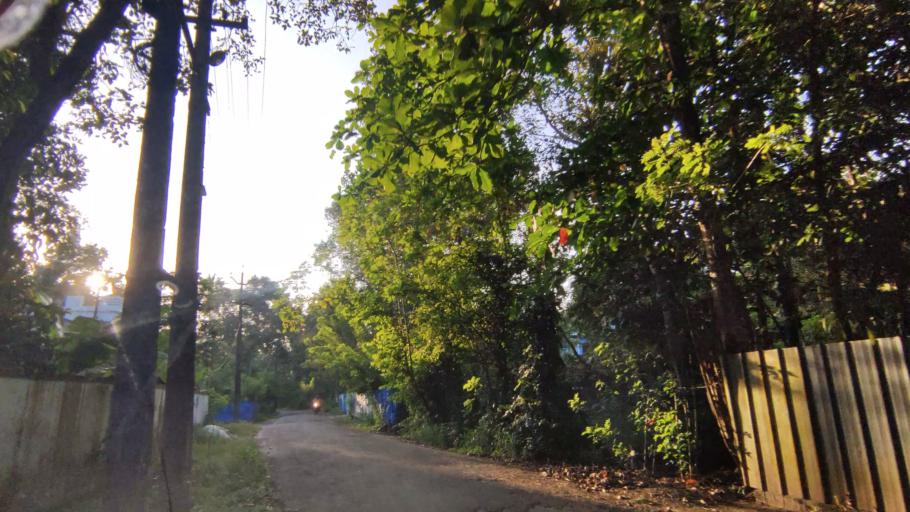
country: IN
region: Kerala
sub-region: Alappuzha
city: Shertallai
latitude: 9.6488
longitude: 76.3649
